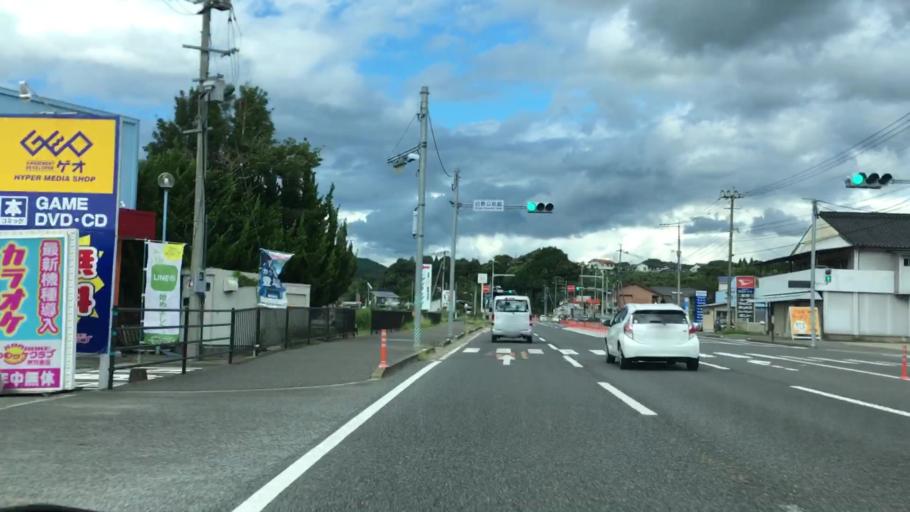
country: JP
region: Saga Prefecture
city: Imaricho-ko
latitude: 33.2744
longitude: 129.8922
